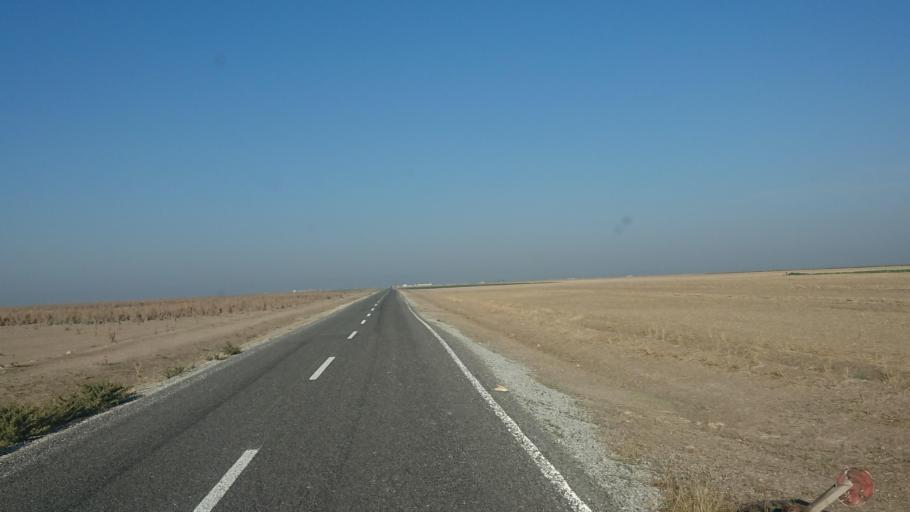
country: TR
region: Aksaray
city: Yesilova
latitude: 38.3879
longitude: 33.7725
